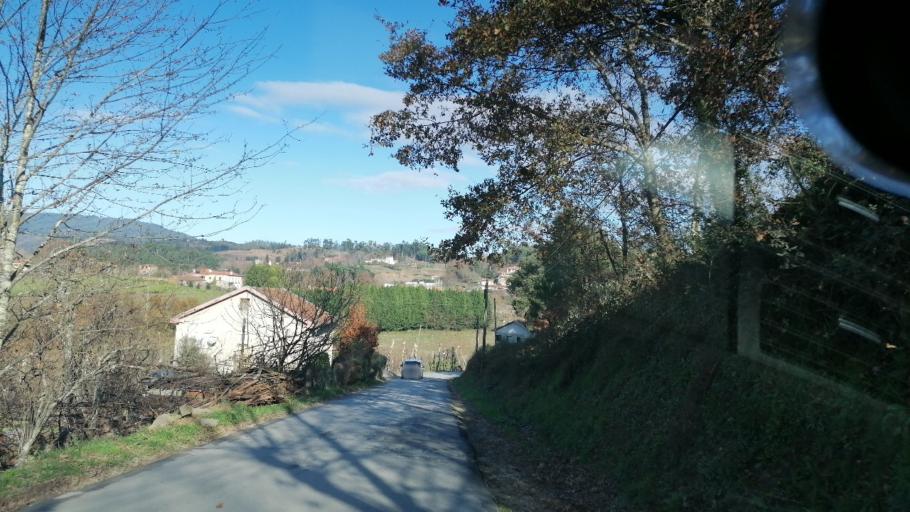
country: PT
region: Vila Real
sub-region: Mondim de Basto
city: Mondim de Basto
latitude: 41.4112
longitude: -7.9810
